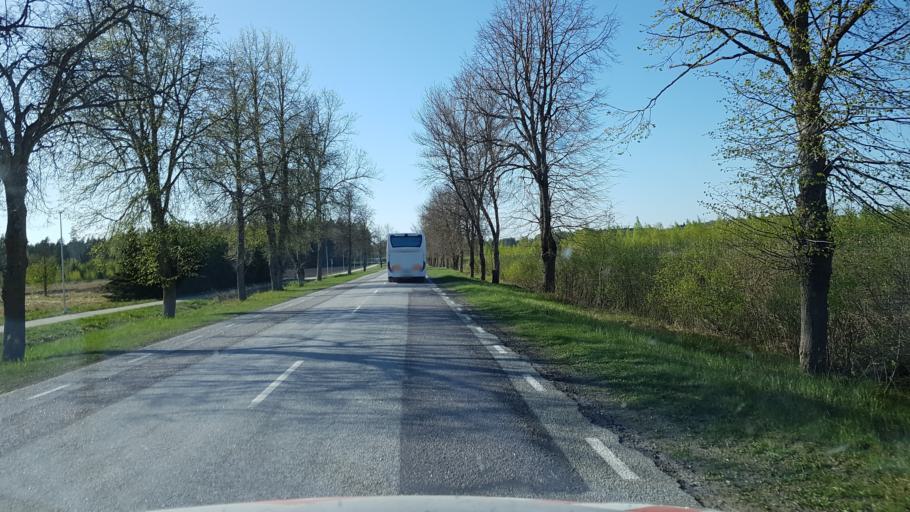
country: EE
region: Paernumaa
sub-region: Paikuse vald
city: Paikuse
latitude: 58.3615
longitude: 24.6514
